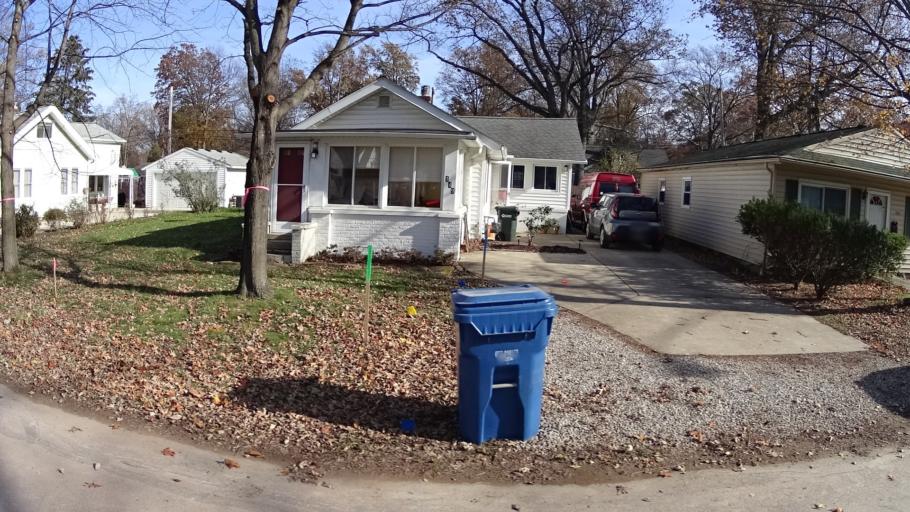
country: US
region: Ohio
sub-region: Lorain County
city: Avon Lake
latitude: 41.5050
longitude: -81.9850
